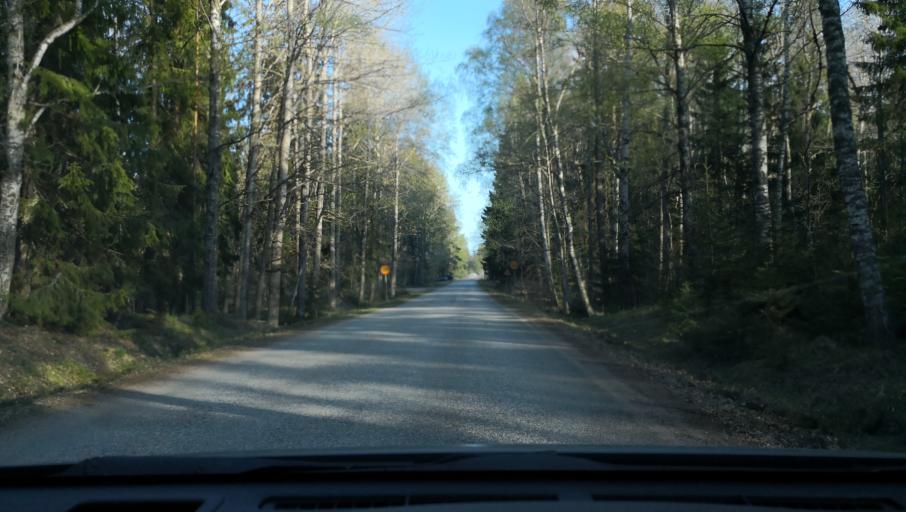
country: SE
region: Uppsala
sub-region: Heby Kommun
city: Tarnsjo
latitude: 60.2716
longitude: 16.9057
